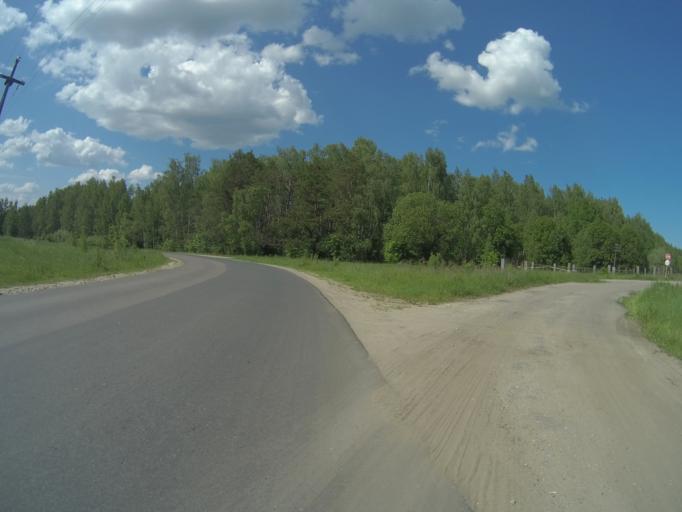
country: RU
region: Vladimir
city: Orgtrud
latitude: 56.2506
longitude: 40.5822
